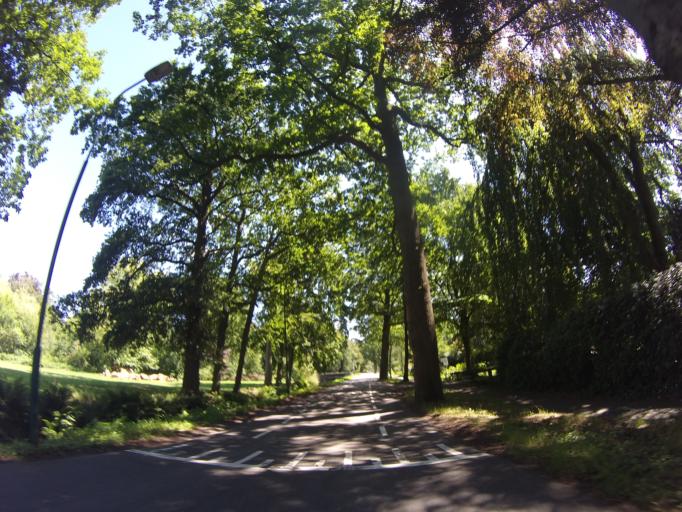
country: NL
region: Utrecht
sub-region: Gemeente De Bilt
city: De Bilt
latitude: 52.1226
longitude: 5.1549
